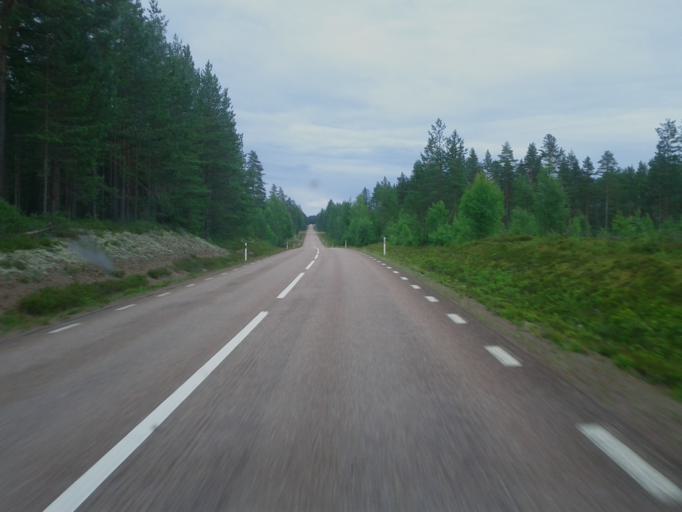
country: SE
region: Dalarna
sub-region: Mora Kommun
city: Mora
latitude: 61.0740
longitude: 14.3561
